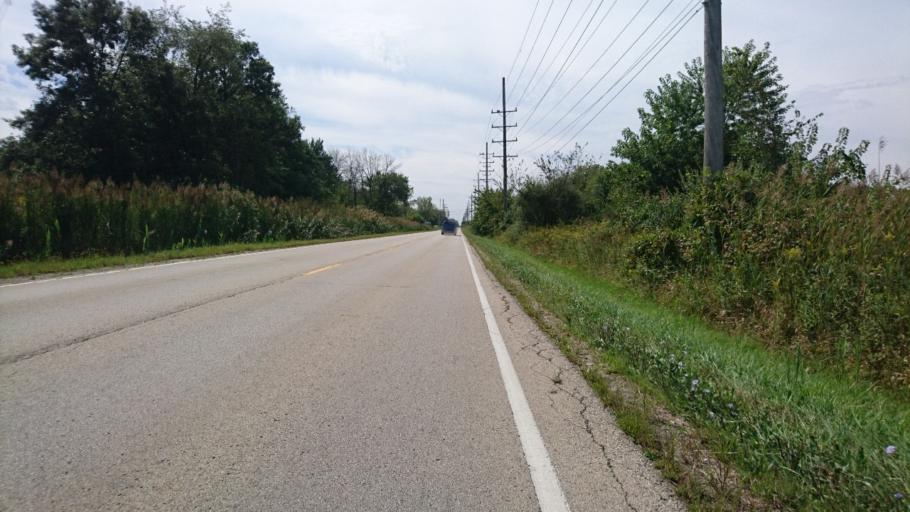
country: US
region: Illinois
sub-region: Will County
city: Wilmington
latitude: 41.2971
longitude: -88.1700
